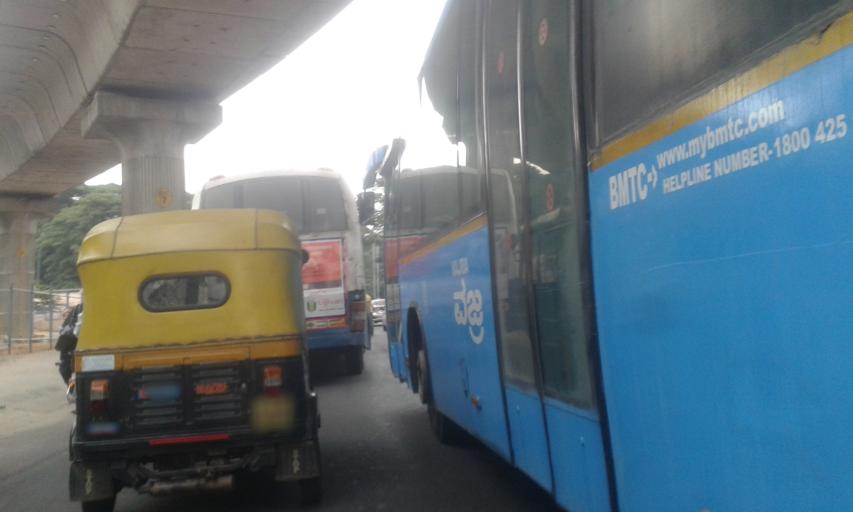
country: IN
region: Karnataka
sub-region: Bangalore Urban
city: Bangalore
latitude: 12.9171
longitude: 77.5792
